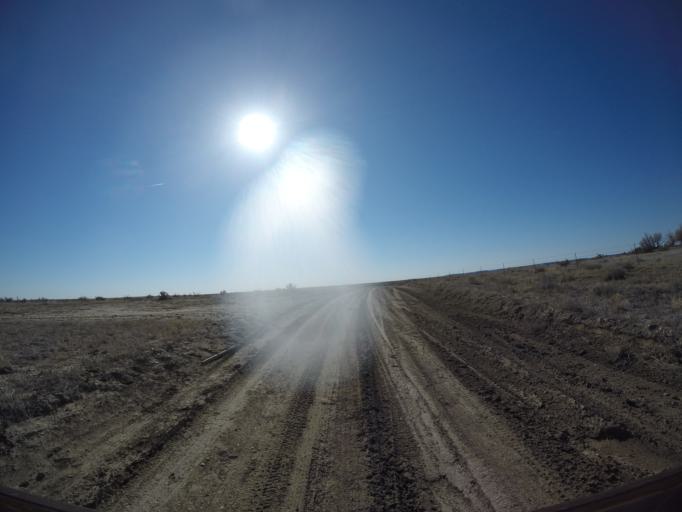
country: US
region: Colorado
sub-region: Otero County
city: La Junta
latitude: 37.6874
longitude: -103.6203
